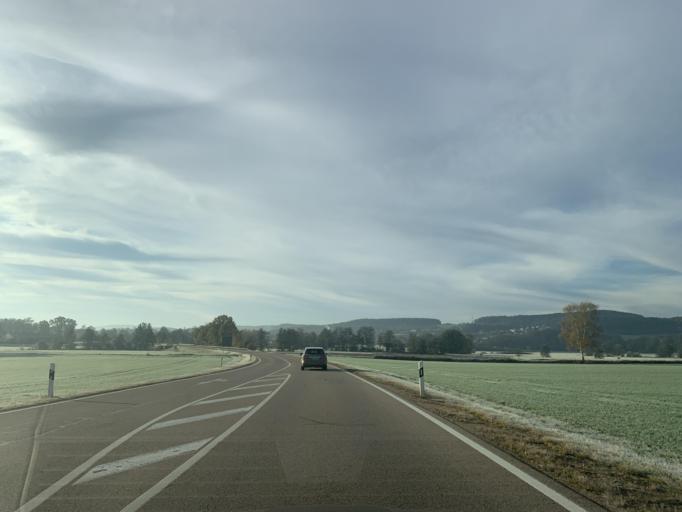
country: DE
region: Bavaria
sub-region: Upper Palatinate
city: Pettendorf
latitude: 49.3591
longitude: 12.3745
